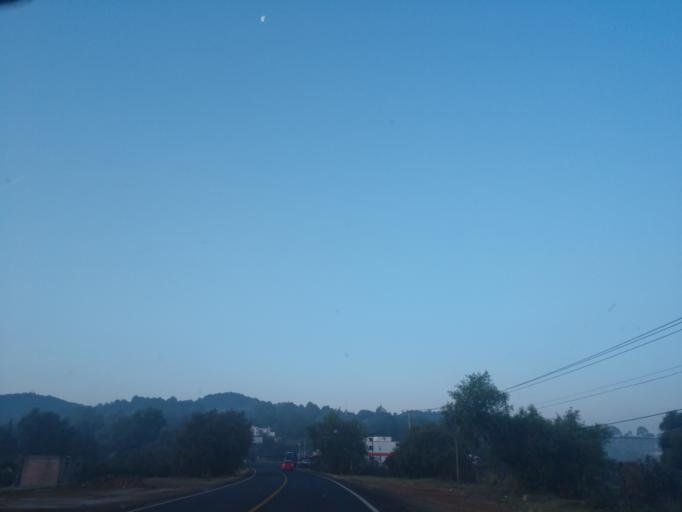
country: MX
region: Jalisco
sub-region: Mazamitla
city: Mazamitla
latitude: 19.9259
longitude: -103.0438
